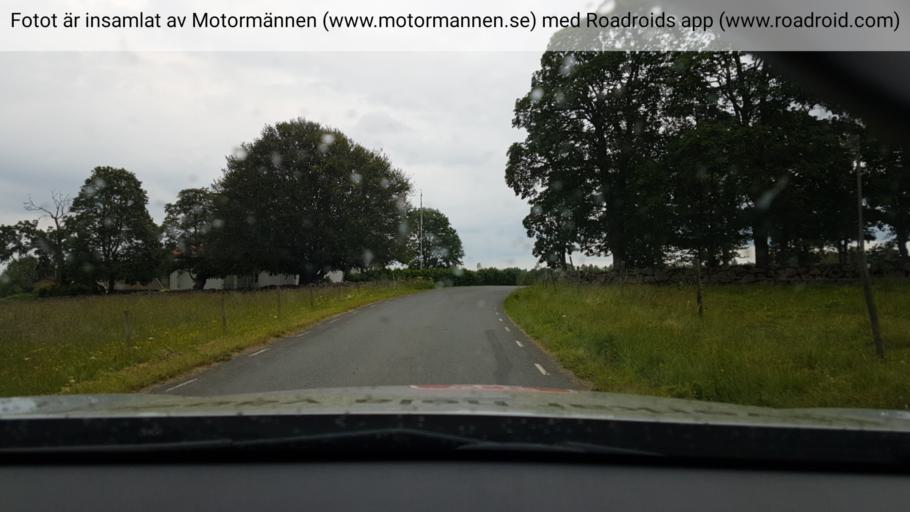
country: SE
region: Joenkoeping
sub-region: Mullsjo Kommun
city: Mullsjoe
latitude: 57.9761
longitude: 13.7564
